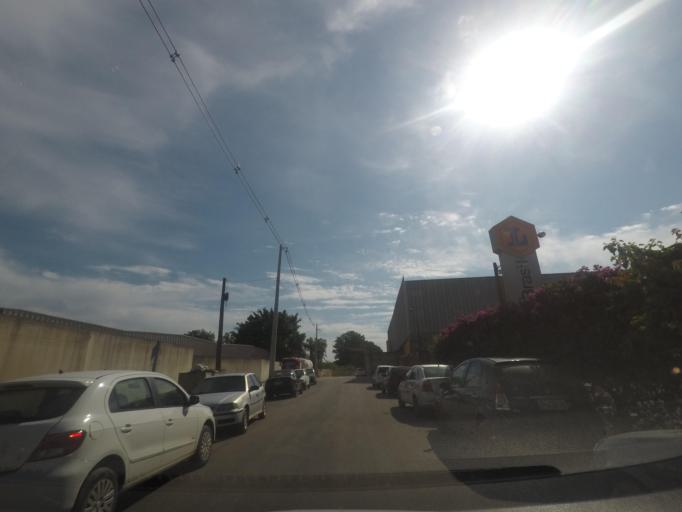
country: BR
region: Sao Paulo
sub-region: Sumare
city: Sumare
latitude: -22.7852
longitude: -47.2325
